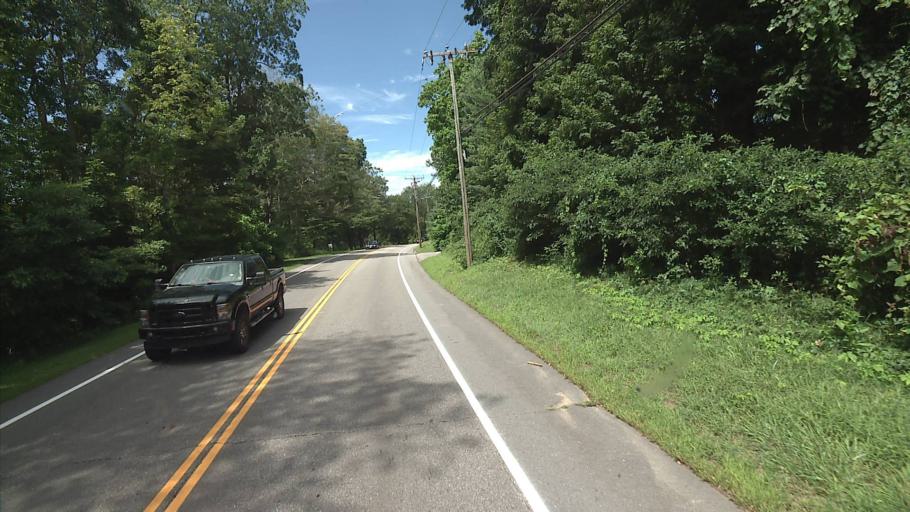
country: US
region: Connecticut
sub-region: Tolland County
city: Storrs
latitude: 41.7938
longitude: -72.2346
